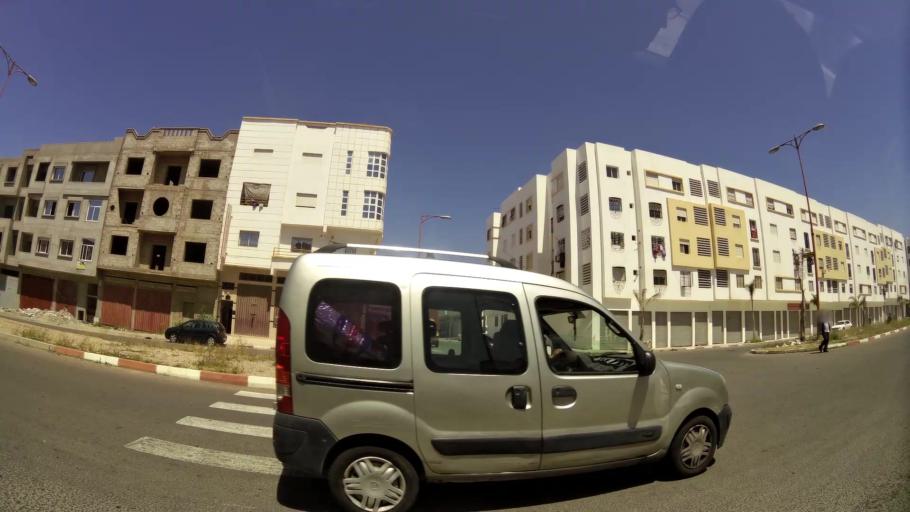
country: MA
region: Oued ed Dahab-Lagouira
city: Dakhla
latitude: 30.4355
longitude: -9.5522
